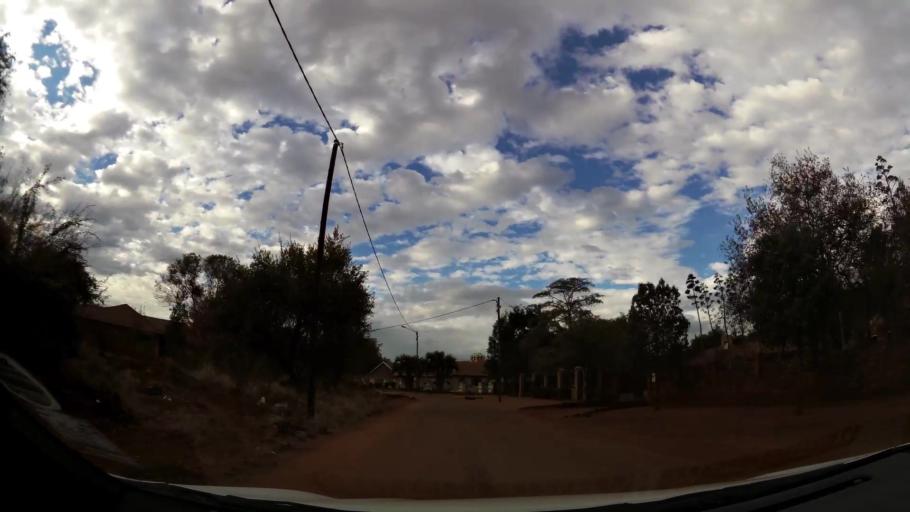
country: ZA
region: Limpopo
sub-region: Waterberg District Municipality
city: Modimolle
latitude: -24.5084
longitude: 28.7244
